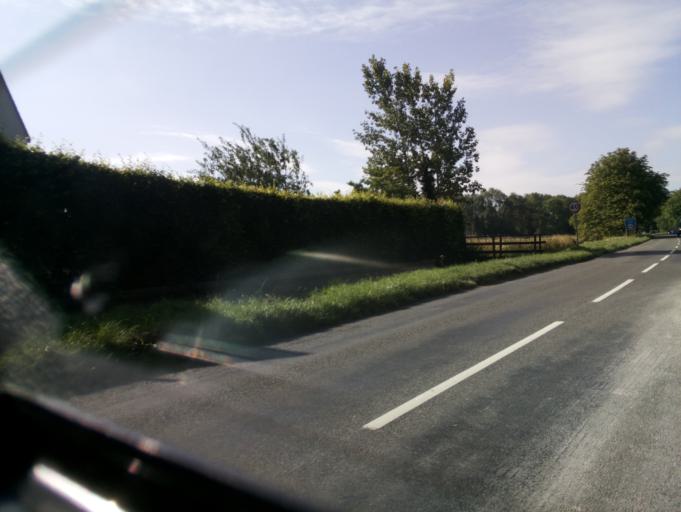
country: GB
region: England
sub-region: Oxfordshire
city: Bampton
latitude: 51.7087
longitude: -1.5911
